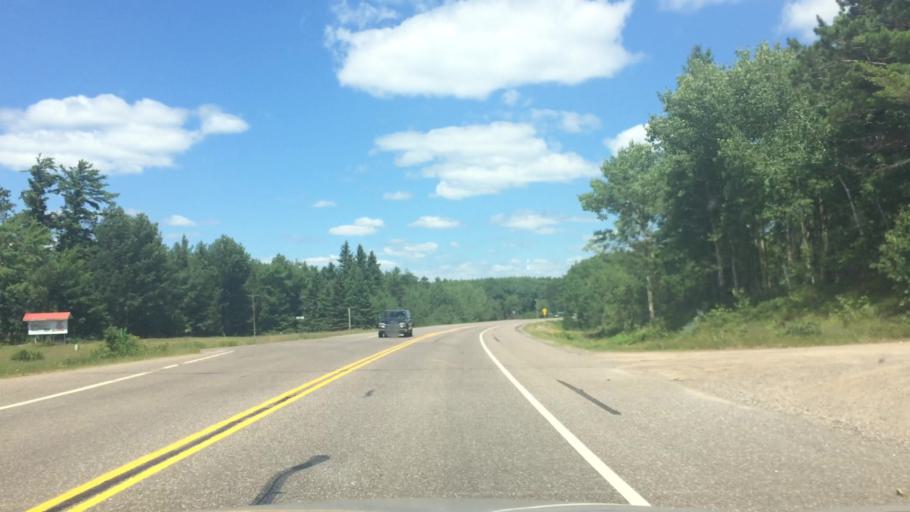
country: US
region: Wisconsin
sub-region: Vilas County
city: Lac du Flambeau
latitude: 45.9486
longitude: -89.7005
